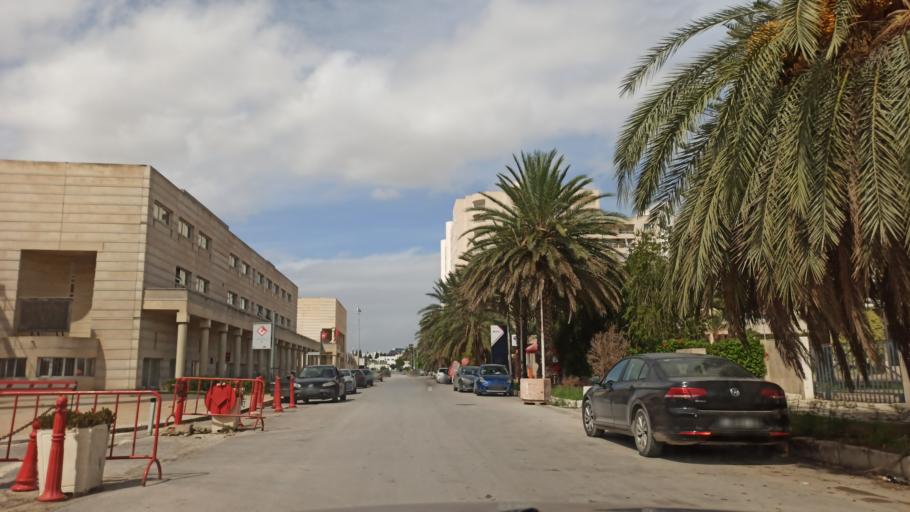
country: TN
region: Ariana
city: Ariana
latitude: 36.8473
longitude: 10.1906
